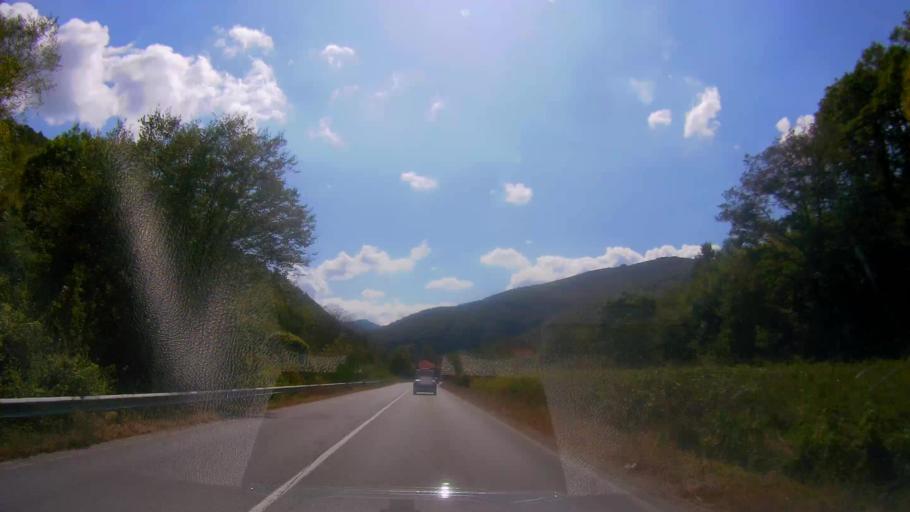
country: BG
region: Stara Zagora
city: Gurkovo
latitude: 42.7430
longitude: 25.7091
